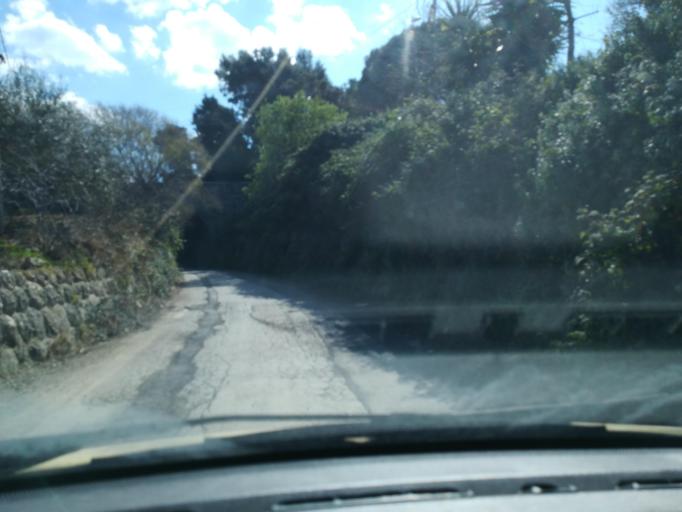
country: IT
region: Sicily
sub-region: Palermo
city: Cannizzaro-Favara
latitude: 38.0447
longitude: 13.2710
